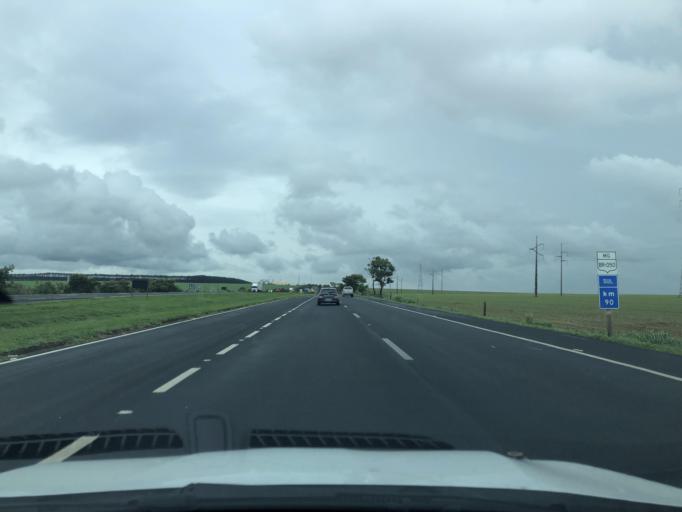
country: BR
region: Minas Gerais
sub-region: Uberlandia
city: Uberlandia
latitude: -19.0501
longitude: -48.1967
